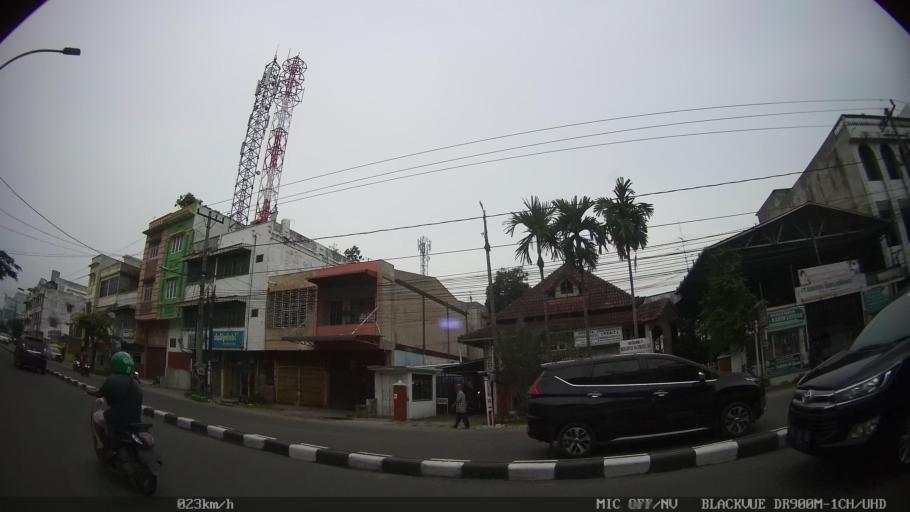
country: ID
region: North Sumatra
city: Medan
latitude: 3.5982
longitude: 98.6937
